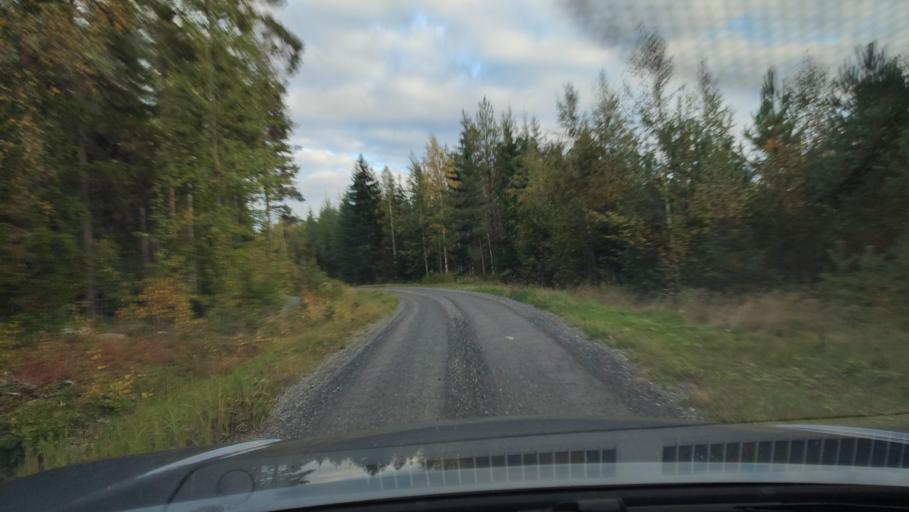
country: FI
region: Ostrobothnia
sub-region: Sydosterbotten
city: Kristinestad
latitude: 62.2322
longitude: 21.4119
